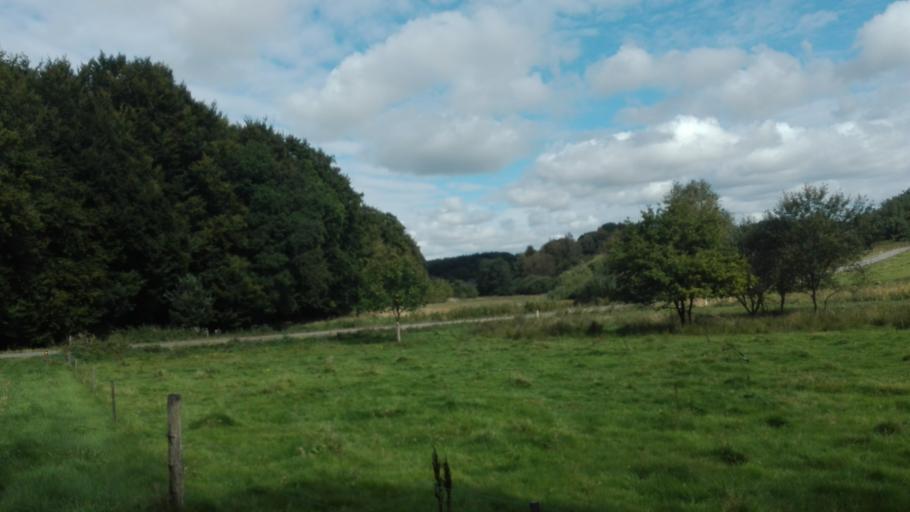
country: DK
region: Central Jutland
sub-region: Skanderborg Kommune
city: Stilling
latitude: 56.0933
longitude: 9.9802
